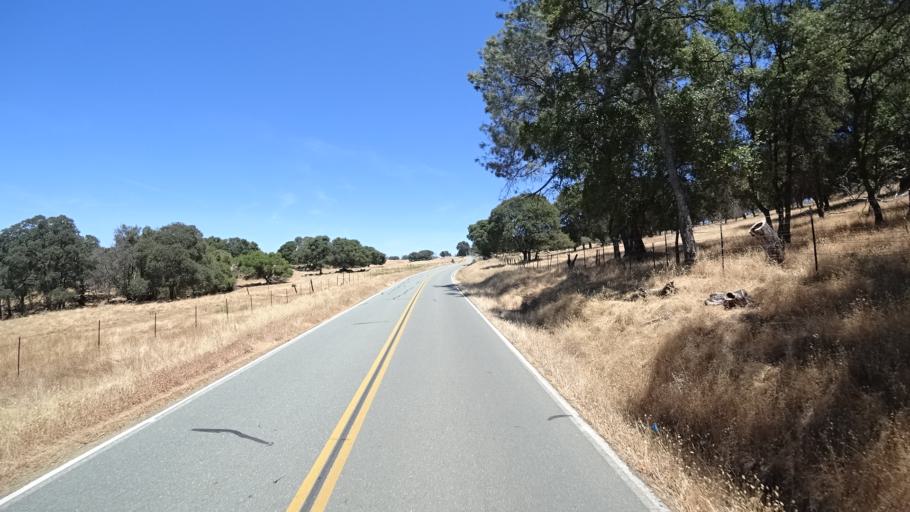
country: US
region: California
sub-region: Amador County
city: Jackson
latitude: 38.2591
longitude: -120.7568
